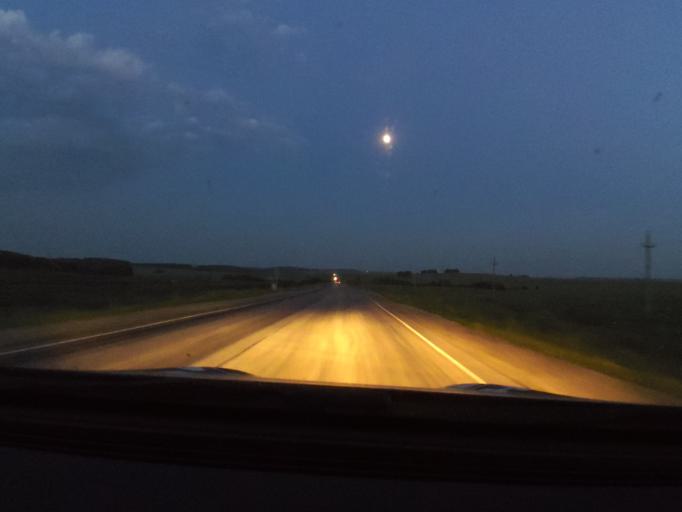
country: RU
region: Bashkortostan
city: Duvan
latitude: 55.9464
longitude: 58.1972
